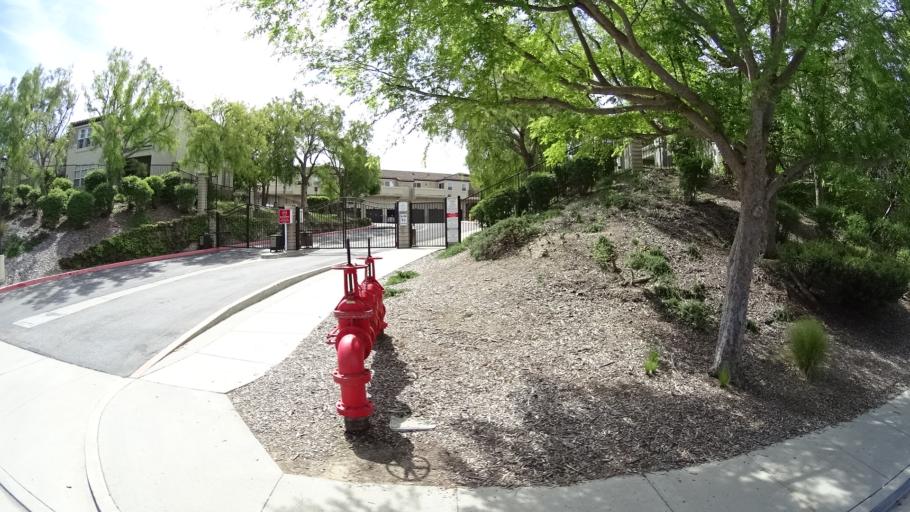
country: US
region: California
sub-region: Ventura County
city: Casa Conejo
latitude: 34.2001
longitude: -118.9233
